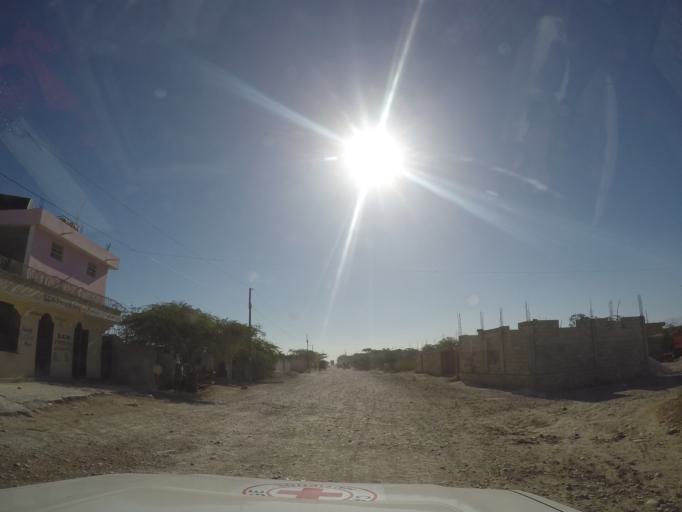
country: HT
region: Ouest
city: Croix des Bouquets
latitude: 18.6501
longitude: -72.2623
